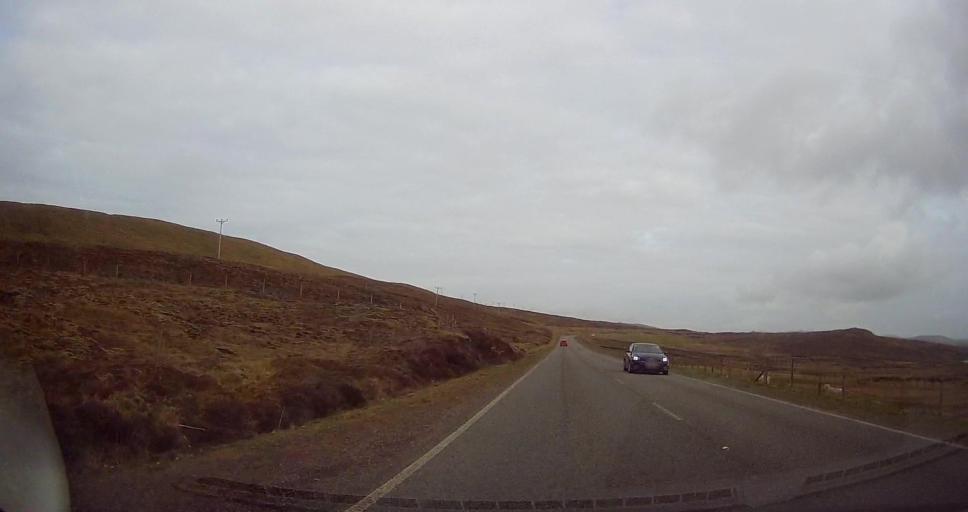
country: GB
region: Scotland
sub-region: Shetland Islands
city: Sandwick
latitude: 60.0803
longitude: -1.2302
